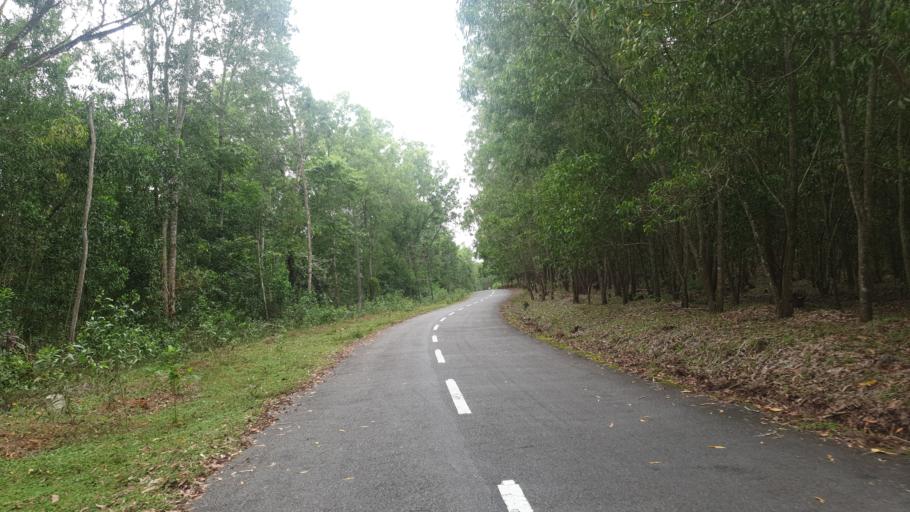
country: IN
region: Kerala
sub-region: Thiruvananthapuram
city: Nedumangad
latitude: 8.6317
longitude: 77.1209
